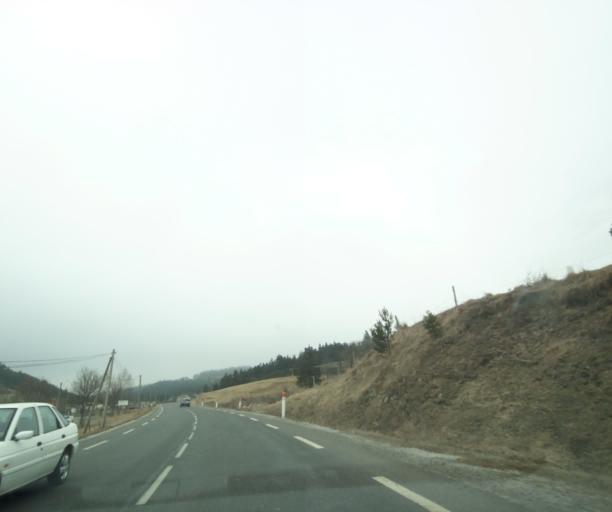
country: FR
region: Languedoc-Roussillon
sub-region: Departement de la Lozere
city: Langogne
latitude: 44.6611
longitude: 3.7567
